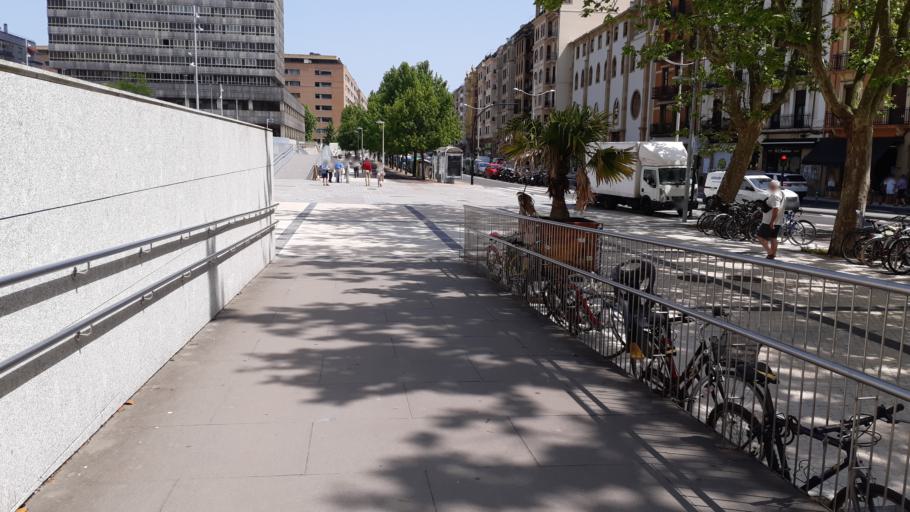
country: ES
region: Basque Country
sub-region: Provincia de Guipuzcoa
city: San Sebastian
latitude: 43.3168
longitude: -1.9753
